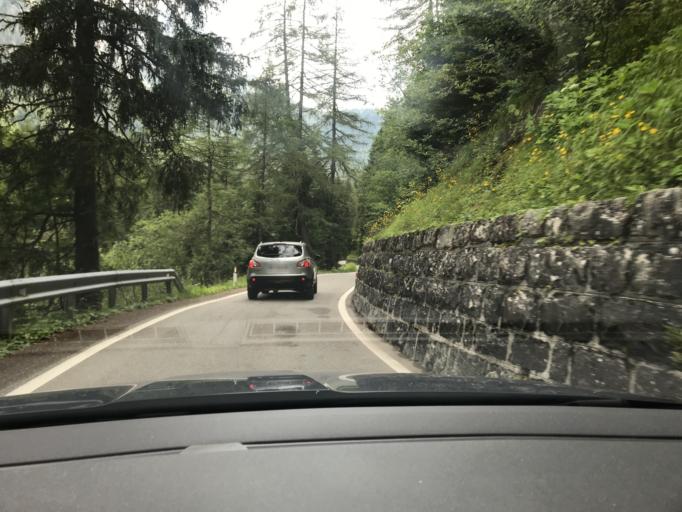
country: IT
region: Trentino-Alto Adige
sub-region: Bolzano
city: San Martino
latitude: 46.8861
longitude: 12.1722
